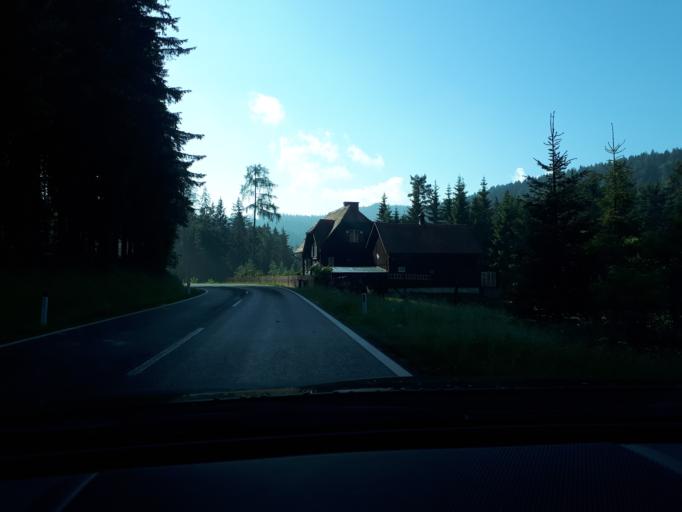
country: AT
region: Styria
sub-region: Politischer Bezirk Voitsberg
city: Pack
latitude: 46.9545
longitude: 14.9768
